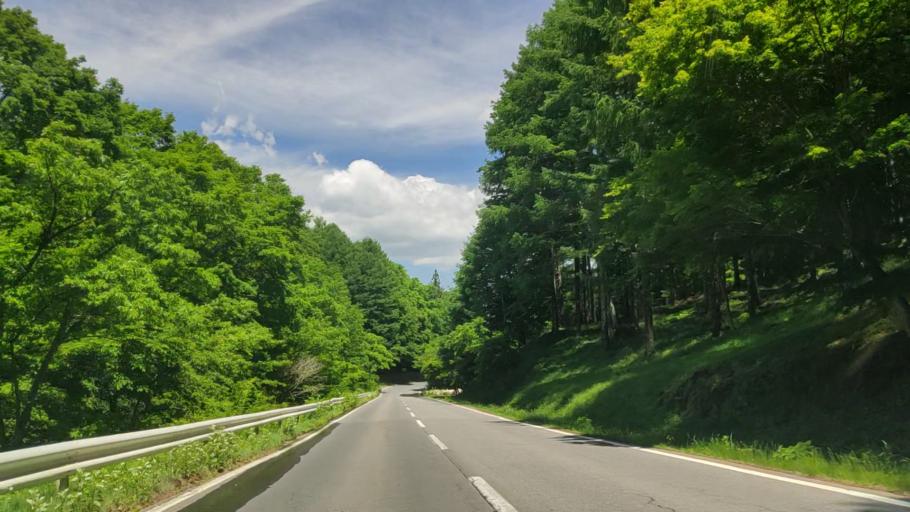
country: JP
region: Nagano
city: Kamimaruko
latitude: 36.1584
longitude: 138.2398
